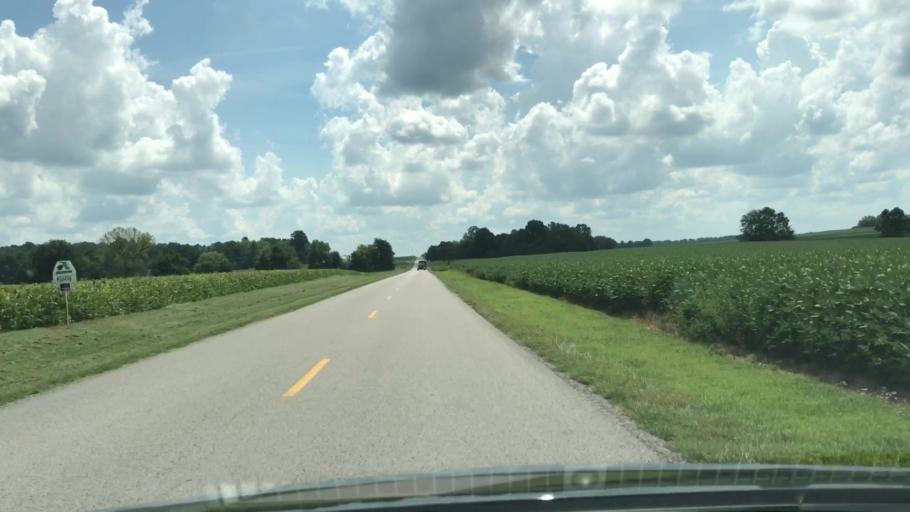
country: US
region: Kentucky
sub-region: Todd County
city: Guthrie
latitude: 36.7040
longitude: -87.0439
